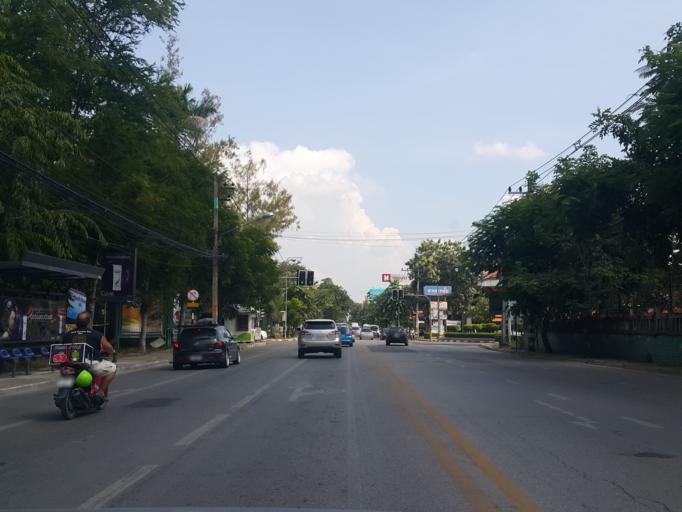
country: TH
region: Chiang Mai
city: Chiang Mai
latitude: 18.7854
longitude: 99.0171
